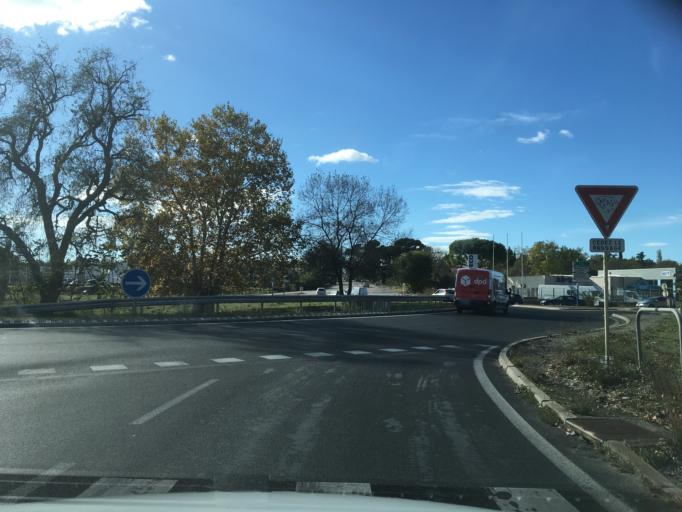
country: FR
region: Languedoc-Roussillon
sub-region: Departement de l'Herault
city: Saint-Jean-de-Vedas
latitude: 43.5842
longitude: 3.8486
